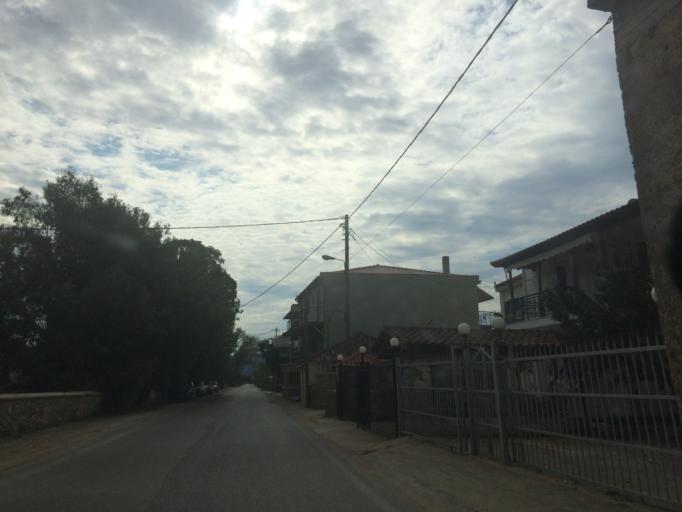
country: GR
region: Peloponnese
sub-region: Nomos Messinias
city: Pylos
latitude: 36.9496
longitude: 21.7037
